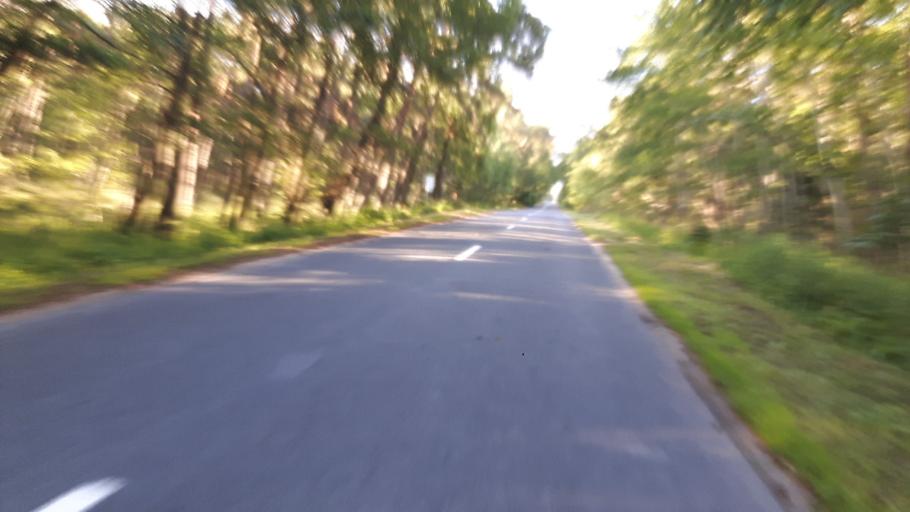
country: LT
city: Nida
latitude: 55.2597
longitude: 20.9383
